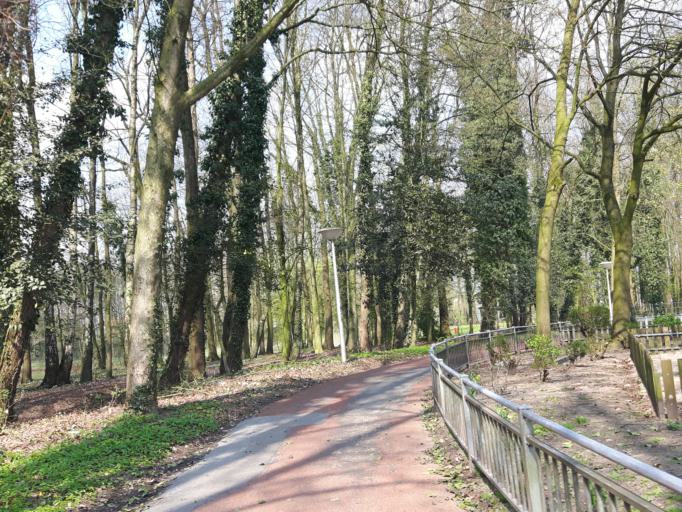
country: NL
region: Overijssel
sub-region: Gemeente Enschede
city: Enschede
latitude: 52.1931
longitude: 6.8520
